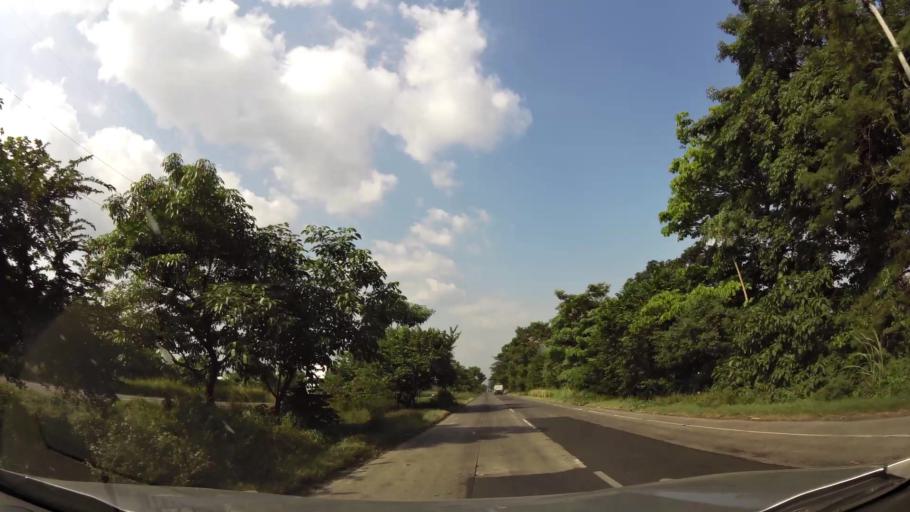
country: GT
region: Escuintla
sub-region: Municipio de Masagua
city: Masagua
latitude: 14.0829
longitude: -90.7782
